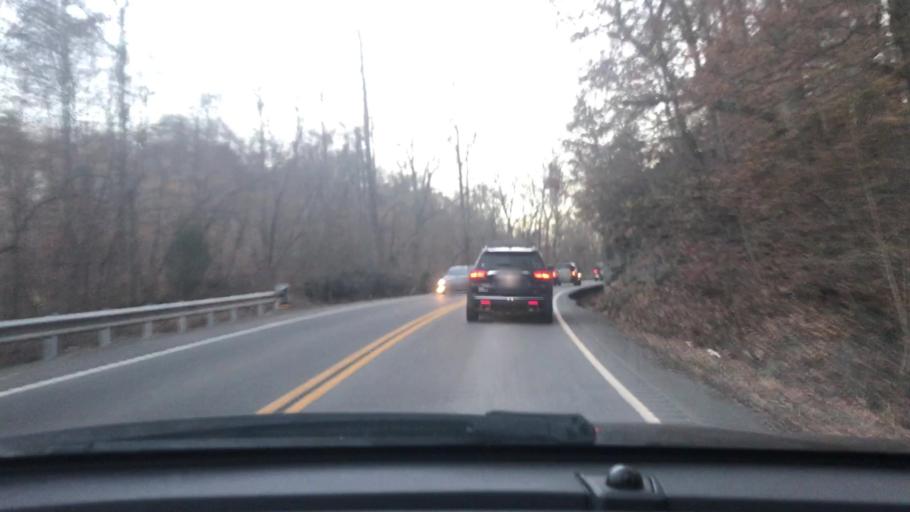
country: US
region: Tennessee
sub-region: Cheatham County
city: Ashland City
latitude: 36.3072
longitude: -87.0443
